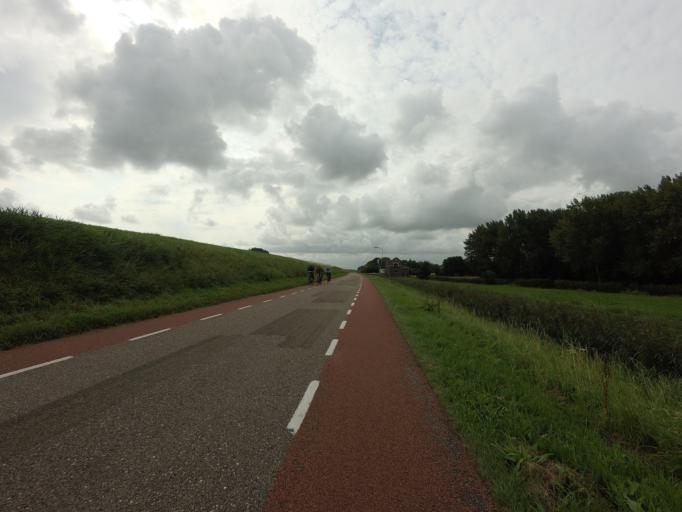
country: NL
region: North Holland
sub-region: Gemeente Hoorn
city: Hoorn
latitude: 52.6265
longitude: 5.0154
